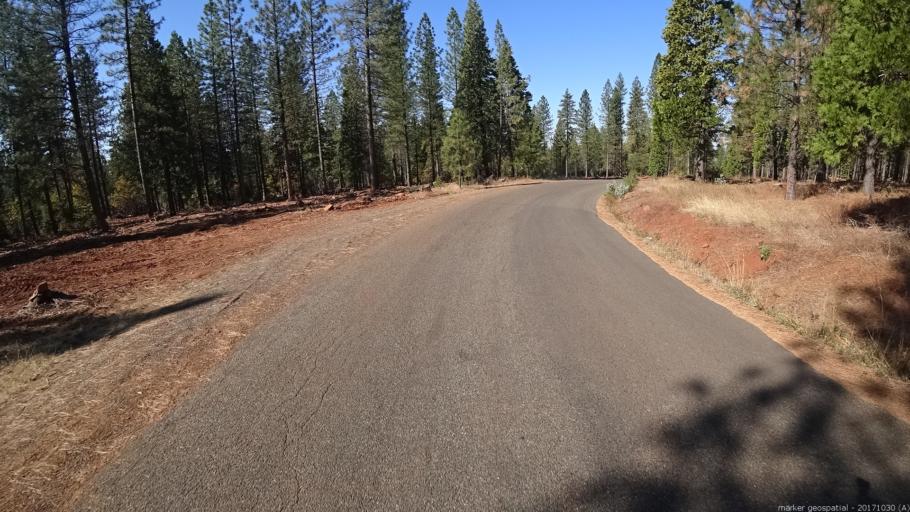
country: US
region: California
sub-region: Shasta County
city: Shingletown
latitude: 40.6157
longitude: -121.8856
